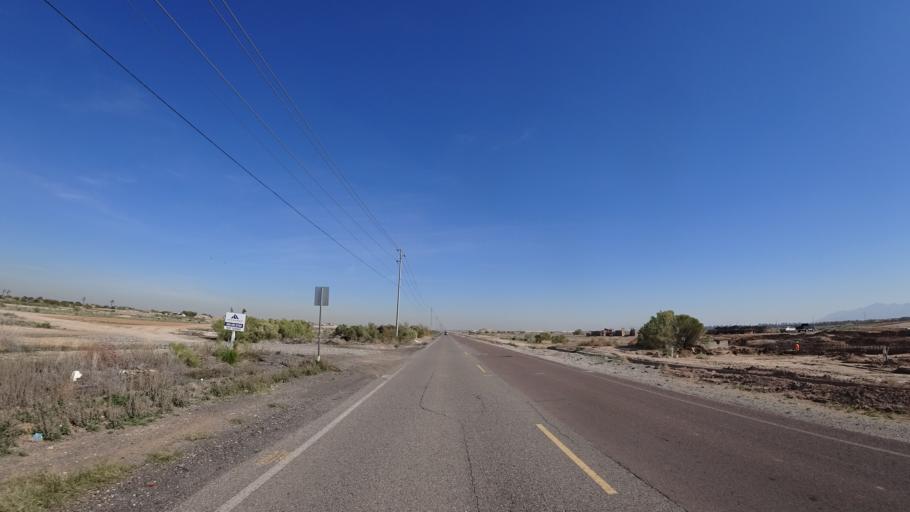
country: US
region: Arizona
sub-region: Maricopa County
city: Citrus Park
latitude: 33.5082
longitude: -112.4530
